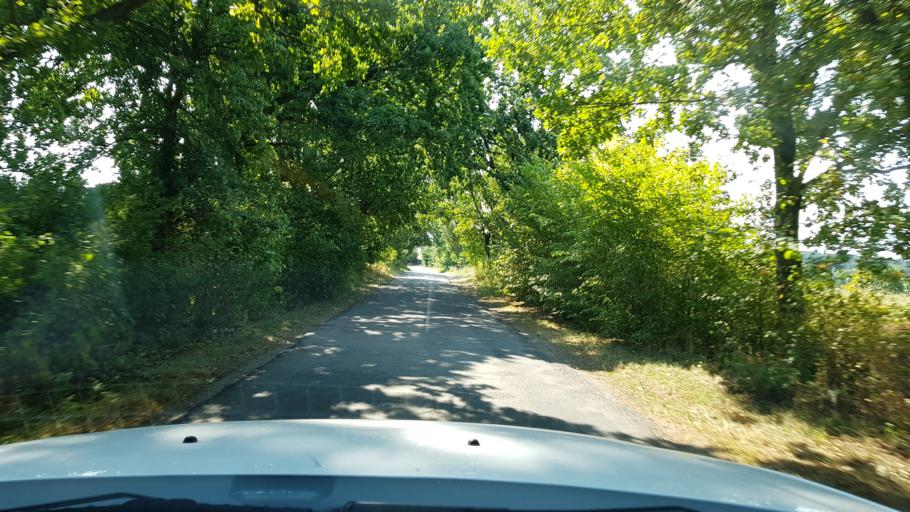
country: PL
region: West Pomeranian Voivodeship
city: Trzcinsko Zdroj
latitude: 52.9260
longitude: 14.5309
